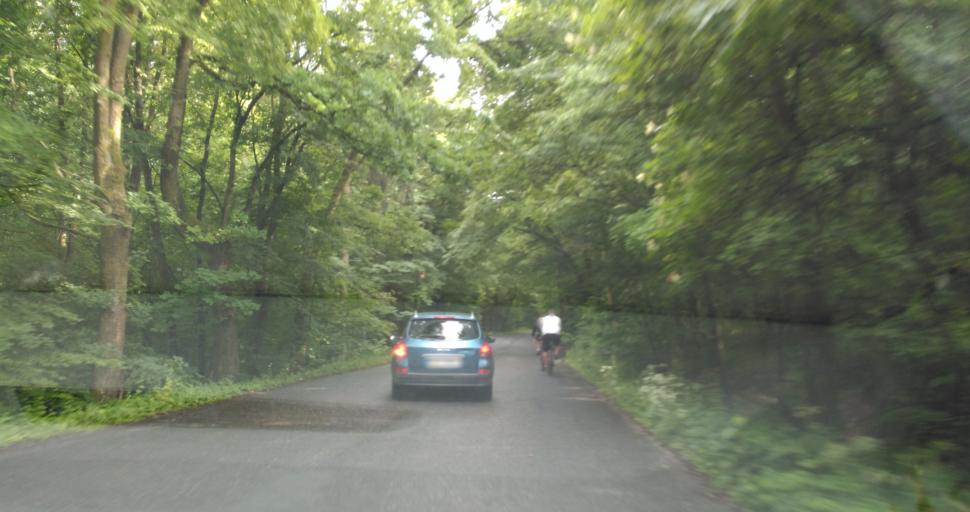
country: CZ
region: Central Bohemia
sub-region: Okres Beroun
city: Beroun
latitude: 49.9050
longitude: 14.0778
